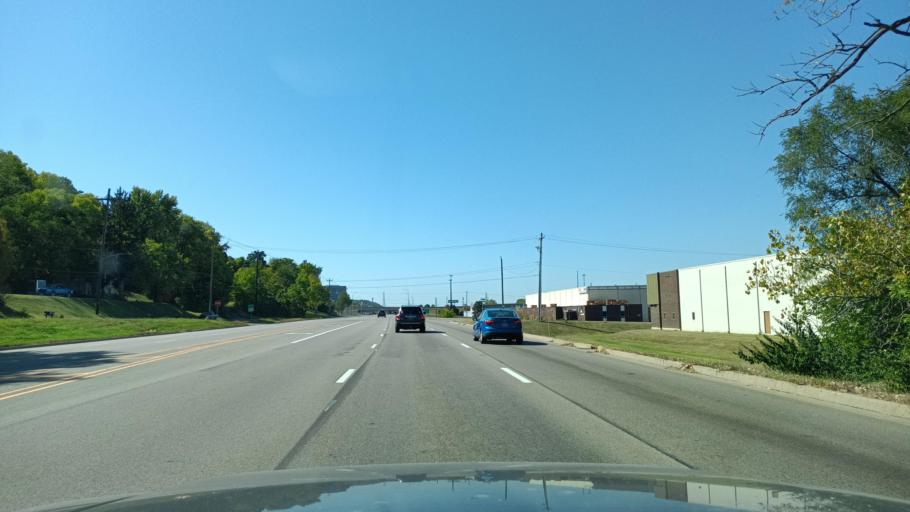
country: US
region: Illinois
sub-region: Tazewell County
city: East Peoria
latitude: 40.6739
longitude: -89.5676
